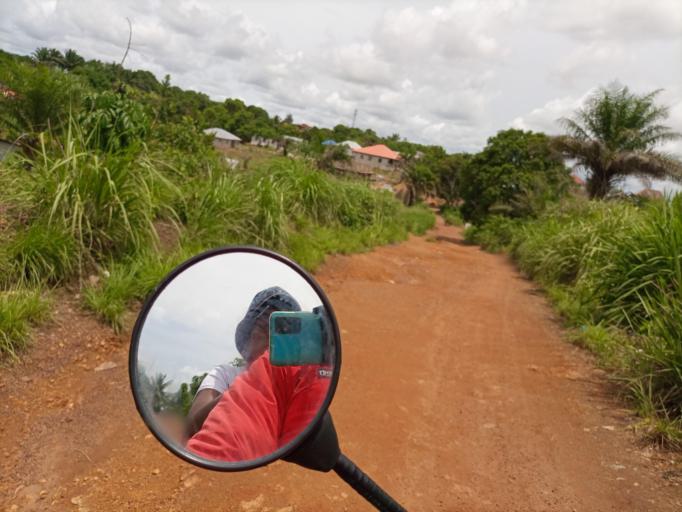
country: SL
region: Southern Province
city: Baoma
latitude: 7.9755
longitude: -11.7133
